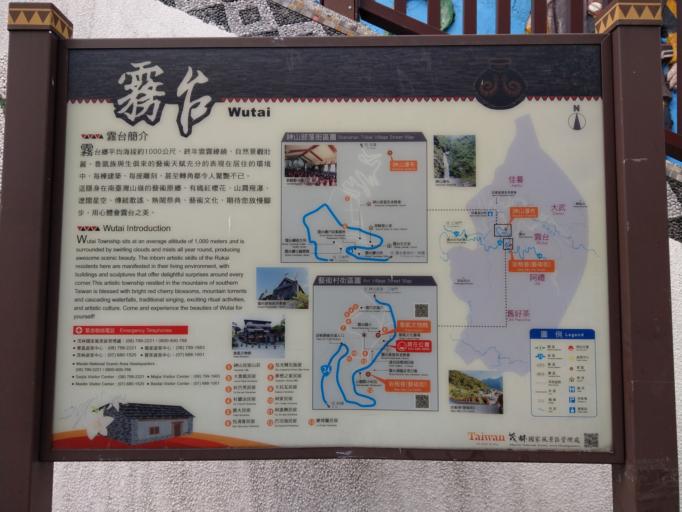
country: TW
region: Taiwan
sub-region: Pingtung
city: Pingtung
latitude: 22.7444
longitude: 120.7322
